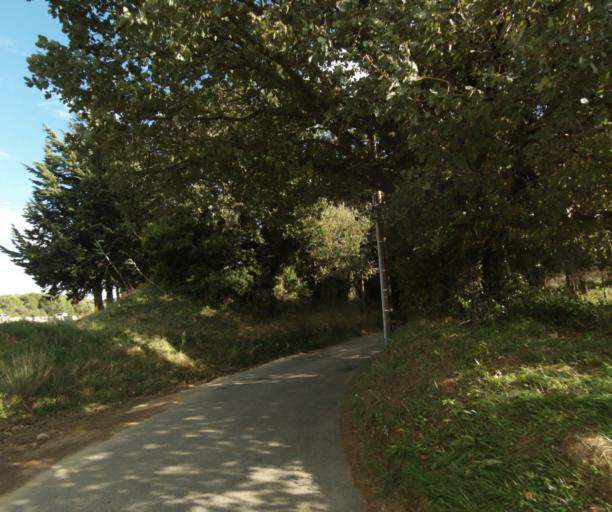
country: FR
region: Languedoc-Roussillon
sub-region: Departement des Pyrenees-Orientales
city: Argelers
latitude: 42.5386
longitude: 3.0245
